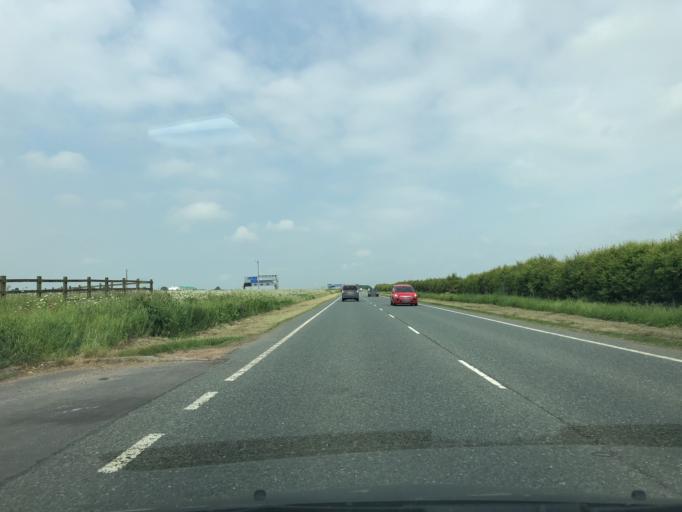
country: GB
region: England
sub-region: North Yorkshire
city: Boroughbridge
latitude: 54.1379
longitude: -1.4250
